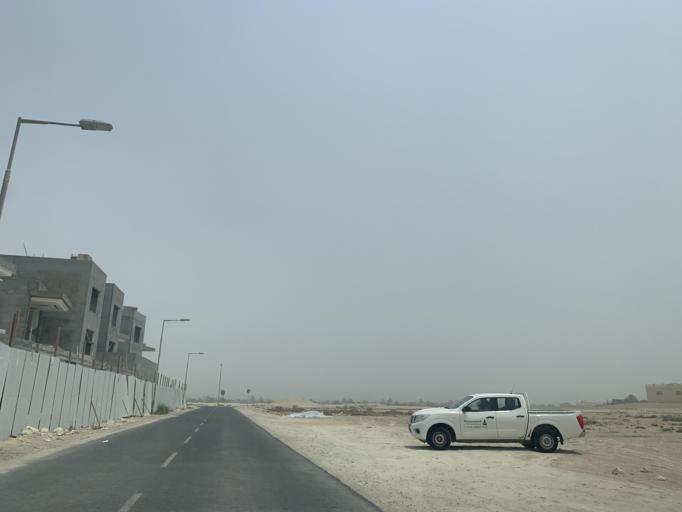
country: BH
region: Central Governorate
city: Madinat Hamad
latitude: 26.1692
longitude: 50.4805
